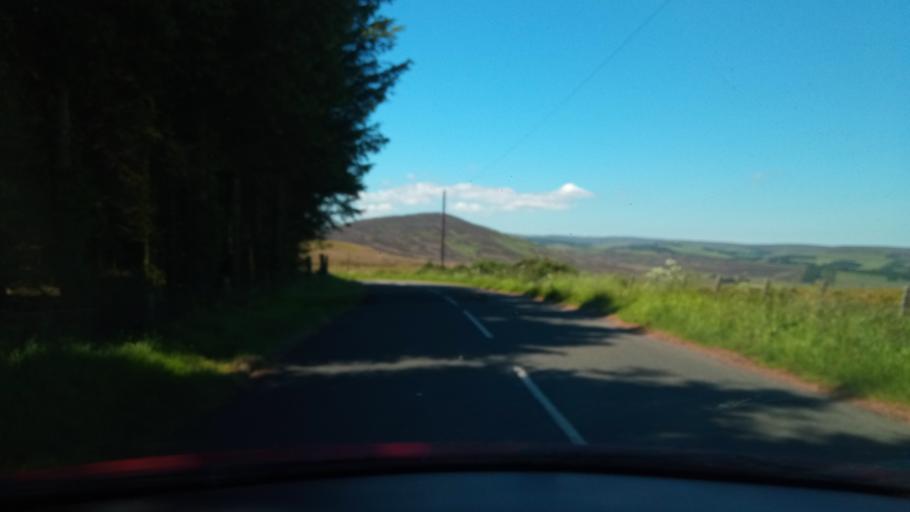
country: GB
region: Scotland
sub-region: The Scottish Borders
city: Duns
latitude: 55.7817
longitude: -2.4399
